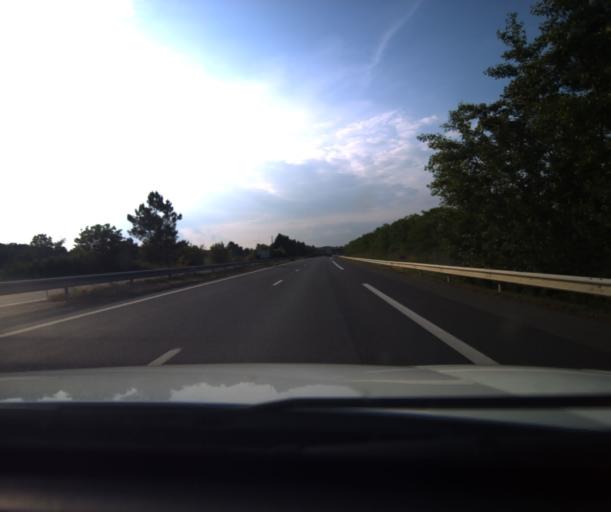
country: FR
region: Midi-Pyrenees
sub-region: Departement du Tarn-et-Garonne
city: Campsas
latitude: 43.9345
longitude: 1.3015
